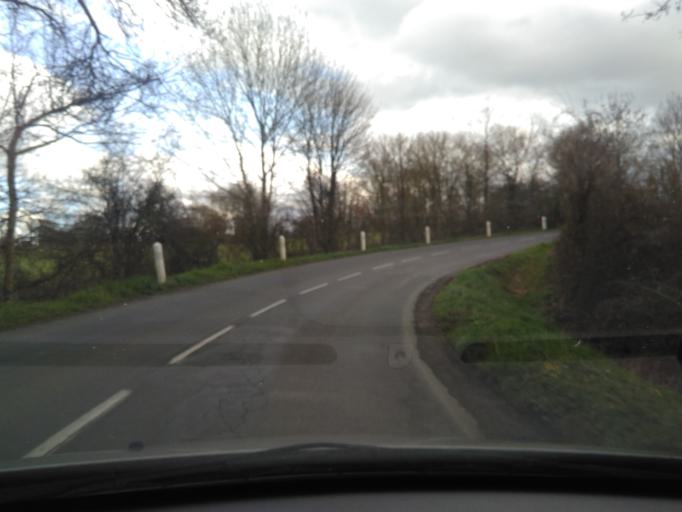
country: FR
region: Pays de la Loire
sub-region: Departement de la Vendee
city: Sainte-Cecile
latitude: 46.6914
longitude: -1.1106
